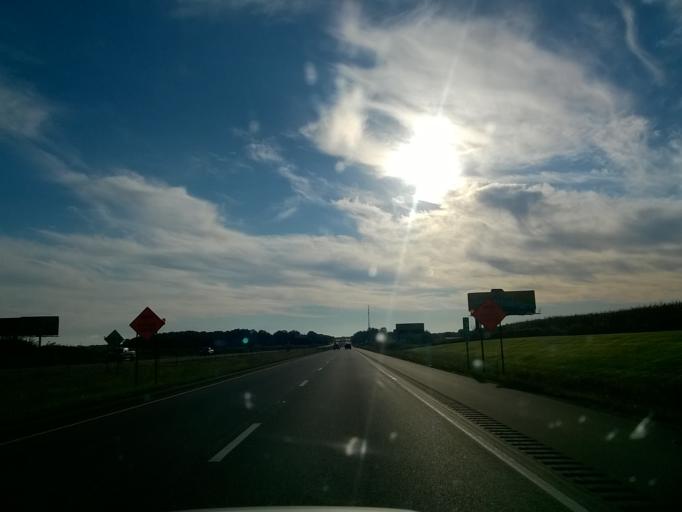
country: US
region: Indiana
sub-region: Gibson County
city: Haubstadt
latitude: 38.1696
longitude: -87.4582
